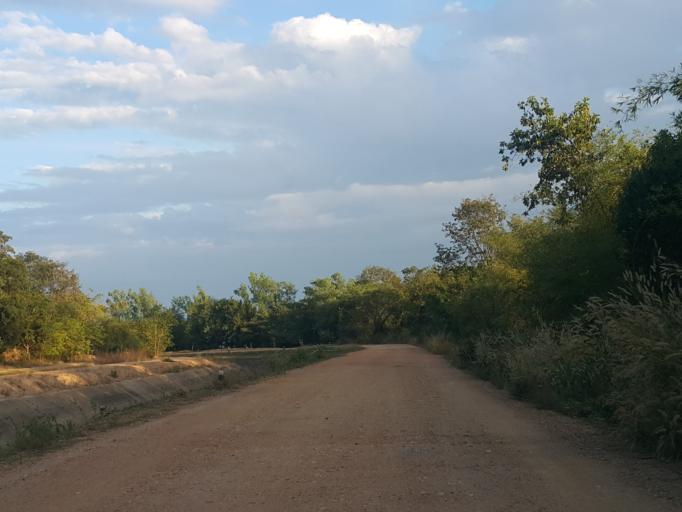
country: TH
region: Lampang
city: Mae Mo
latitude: 18.4339
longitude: 99.6006
